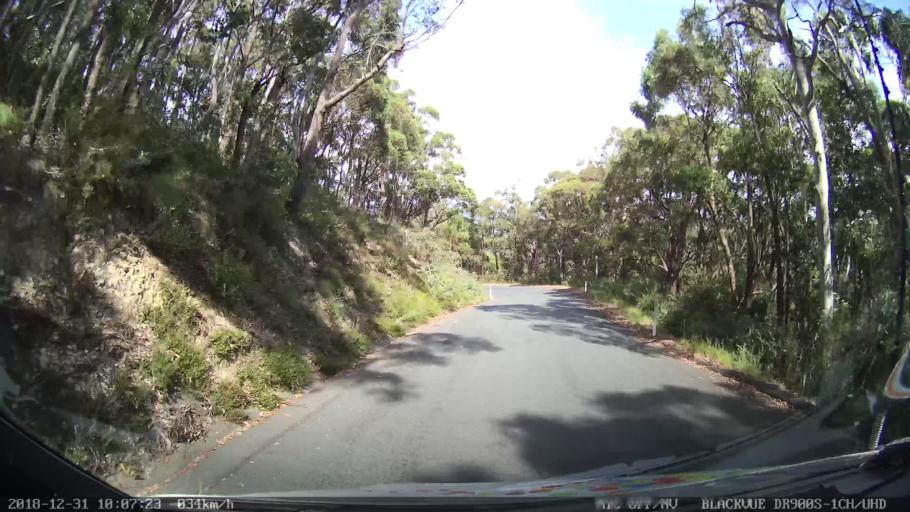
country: AU
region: New South Wales
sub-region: Snowy River
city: Jindabyne
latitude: -36.5315
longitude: 148.1840
